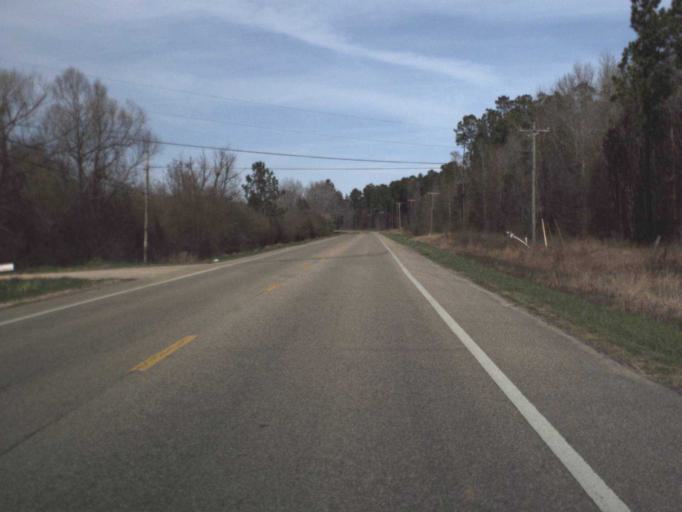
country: US
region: Florida
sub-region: Washington County
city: Chipley
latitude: 30.8442
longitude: -85.5308
